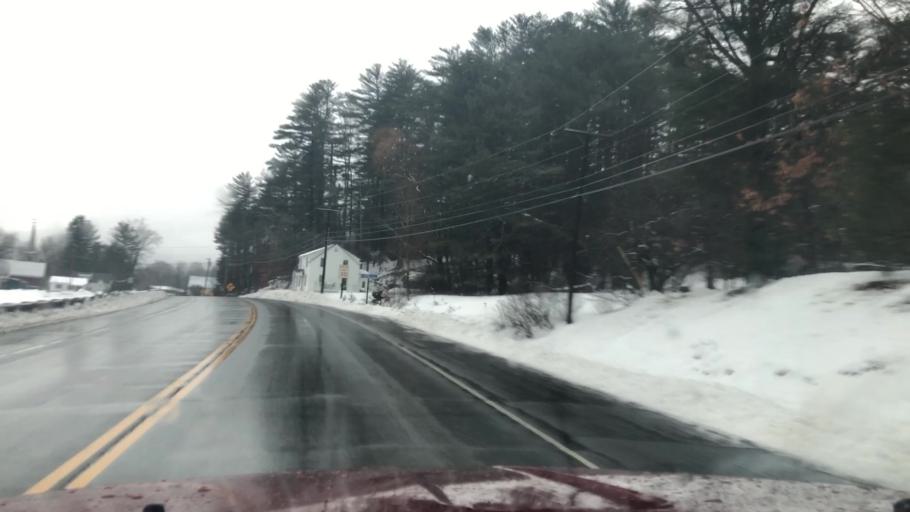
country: US
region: Maine
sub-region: Oxford County
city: Rumford
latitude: 44.4999
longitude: -70.6670
